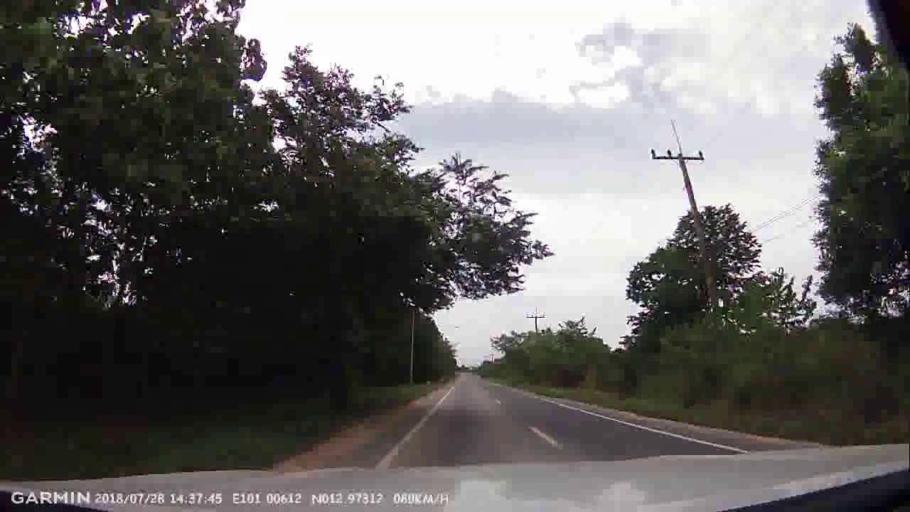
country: TH
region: Chon Buri
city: Ban Talat Bueng
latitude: 12.9734
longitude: 101.0059
